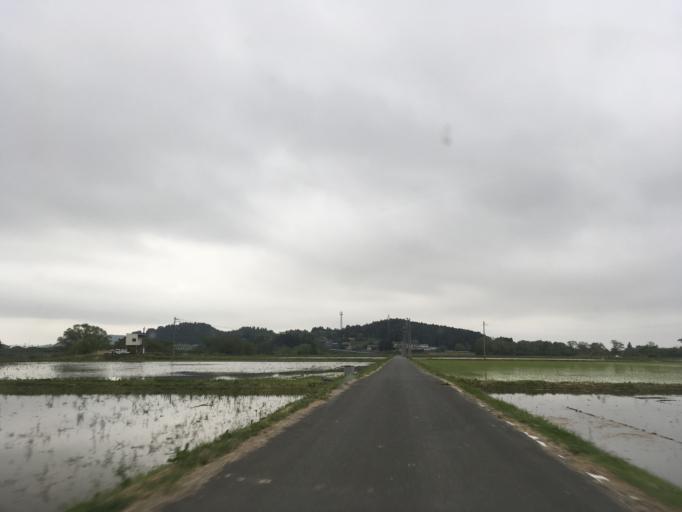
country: JP
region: Miyagi
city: Wakuya
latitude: 38.7154
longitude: 141.2891
